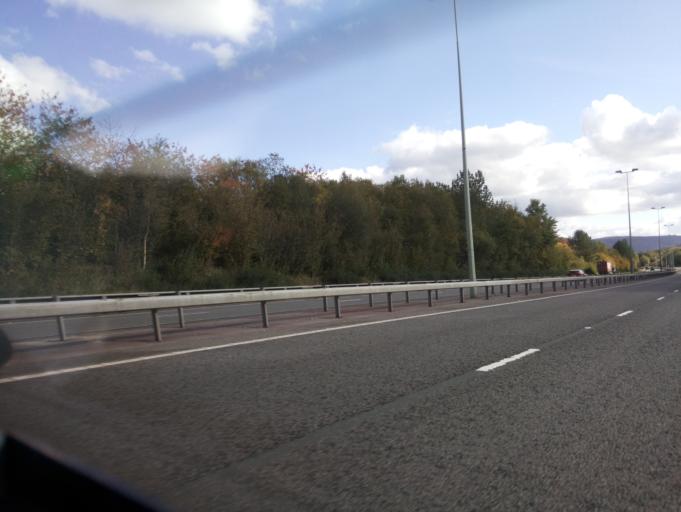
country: GB
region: Wales
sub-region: Merthyr Tydfil County Borough
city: Merthyr Tydfil
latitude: 51.7420
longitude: -3.3878
